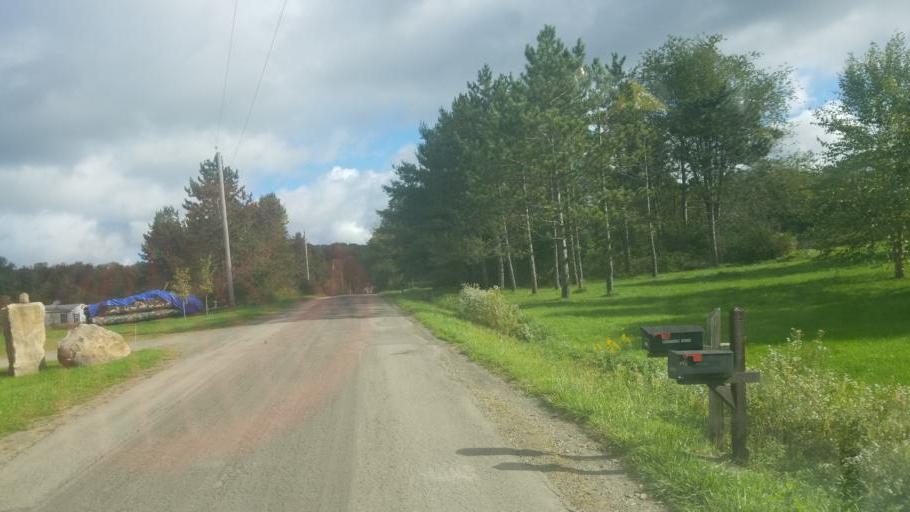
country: US
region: New York
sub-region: Cattaraugus County
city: Weston Mills
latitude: 42.1286
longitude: -78.3030
